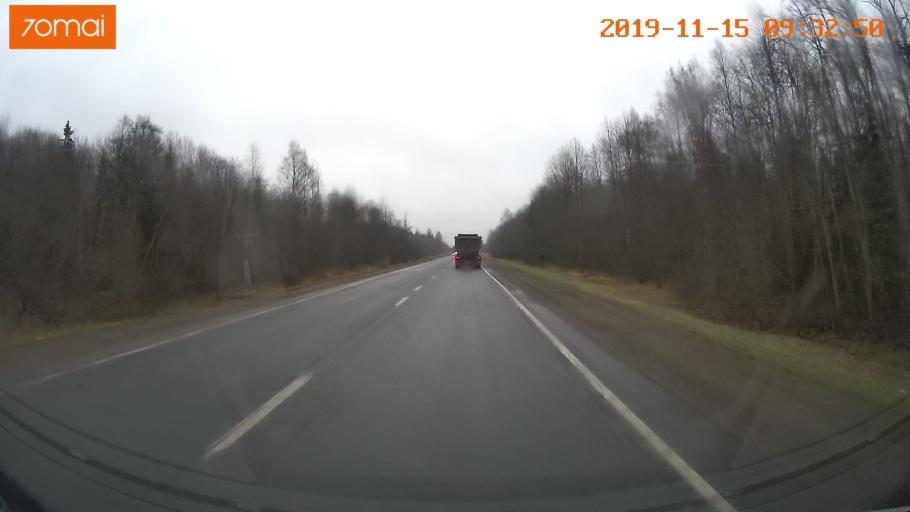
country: RU
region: Vologda
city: Sheksna
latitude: 59.2698
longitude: 38.3446
